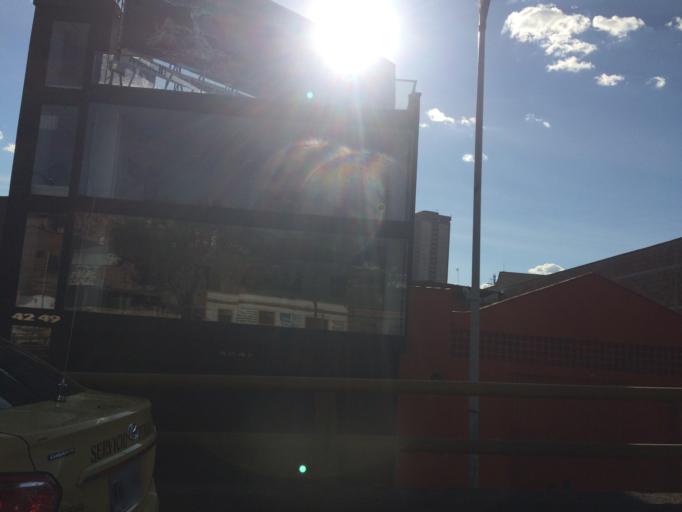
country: CO
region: Antioquia
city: Medellin
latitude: 6.2426
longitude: -75.5691
